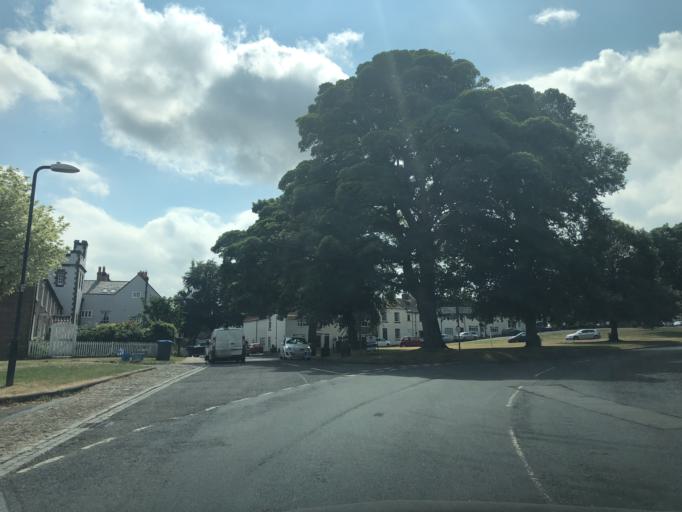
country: GB
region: England
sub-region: North Yorkshire
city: Stokesley
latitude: 54.4509
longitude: -1.2754
